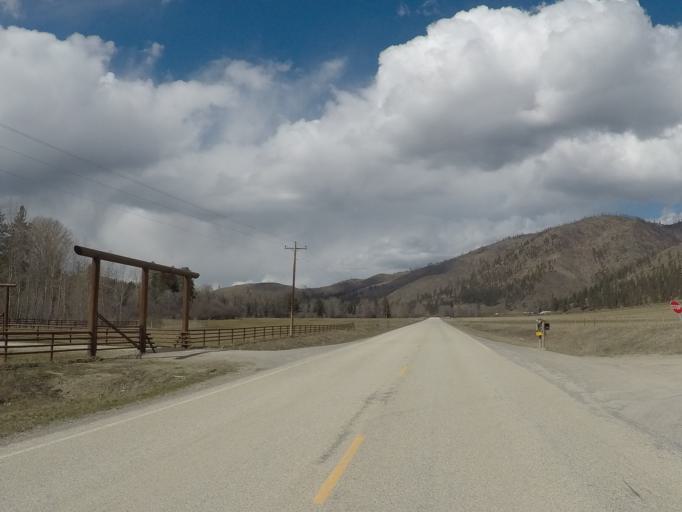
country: US
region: Montana
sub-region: Missoula County
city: Lolo
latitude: 46.7586
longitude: -114.2538
